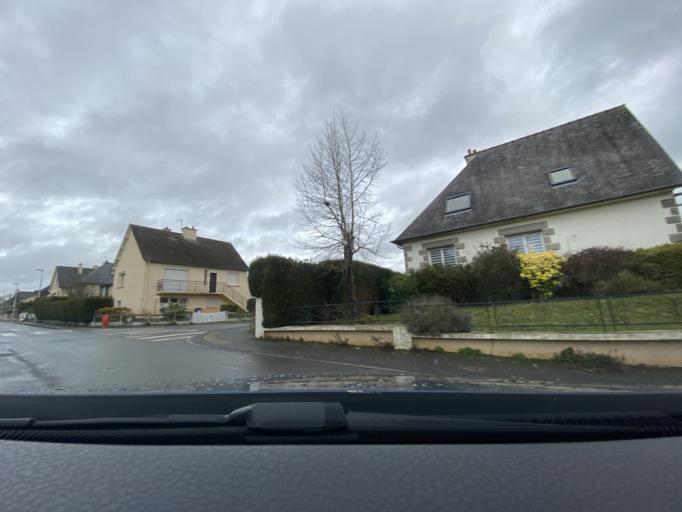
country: FR
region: Brittany
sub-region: Departement d'Ille-et-Vilaine
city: Melesse
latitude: 48.2193
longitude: -1.6961
